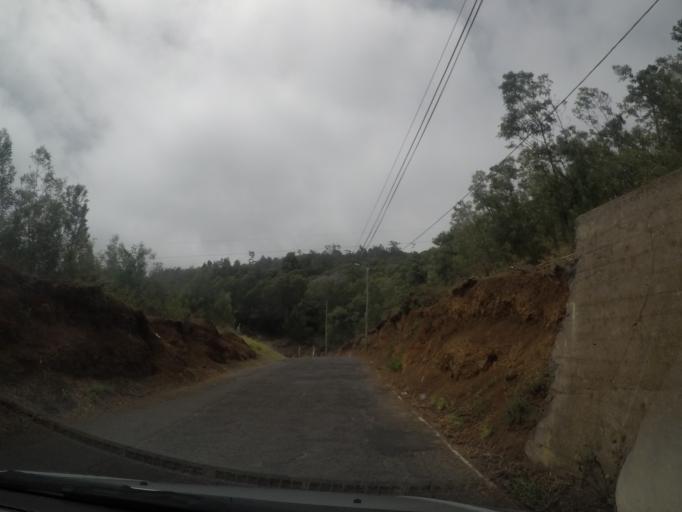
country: PT
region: Madeira
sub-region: Machico
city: Machico
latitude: 32.7024
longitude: -16.7884
